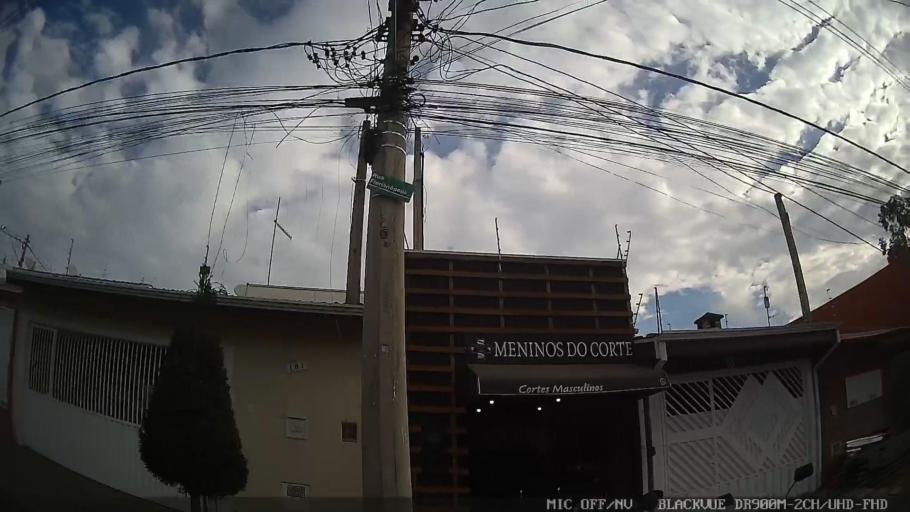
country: BR
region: Sao Paulo
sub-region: Salto
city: Salto
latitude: -23.1822
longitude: -47.2726
